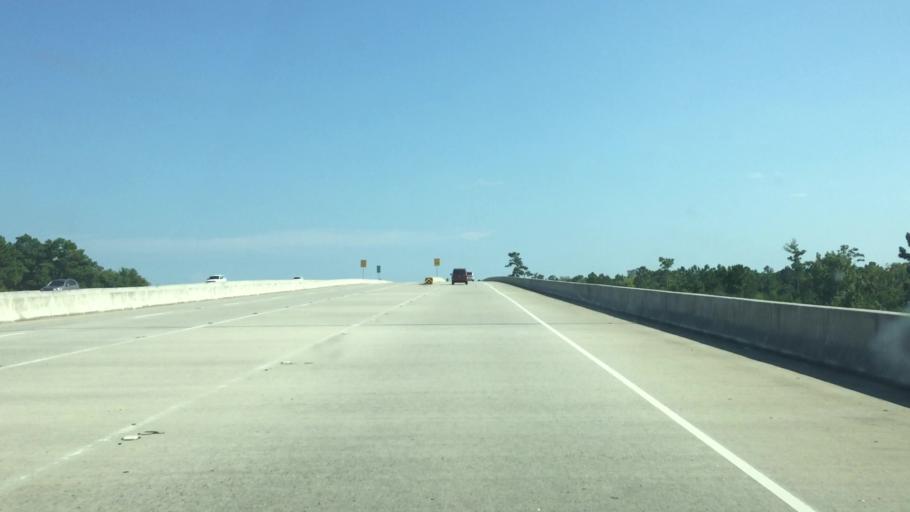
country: US
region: South Carolina
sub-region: Horry County
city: North Myrtle Beach
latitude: 33.7920
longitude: -78.7780
